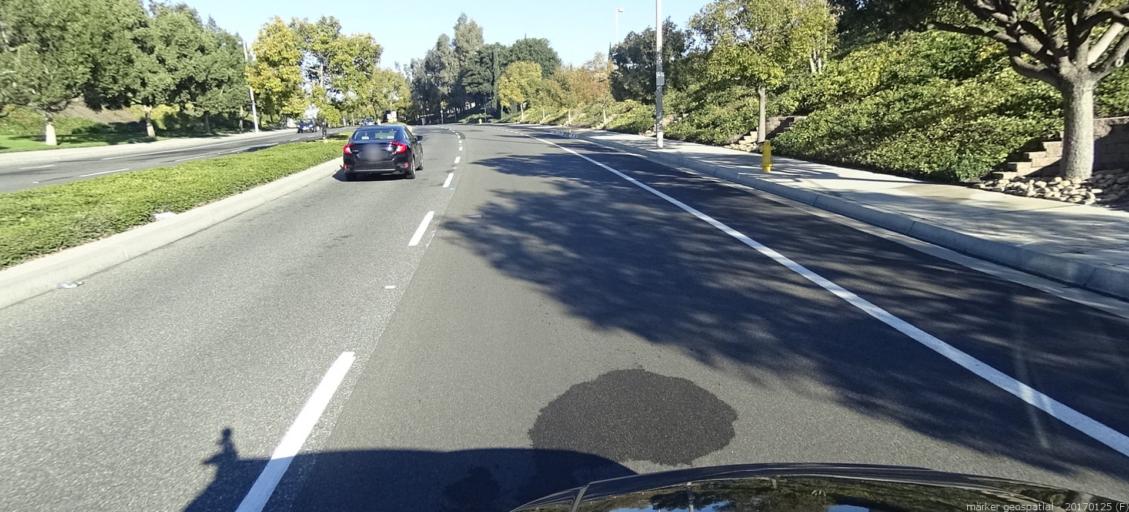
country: US
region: California
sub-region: Orange County
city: Foothill Ranch
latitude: 33.6733
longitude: -117.6709
